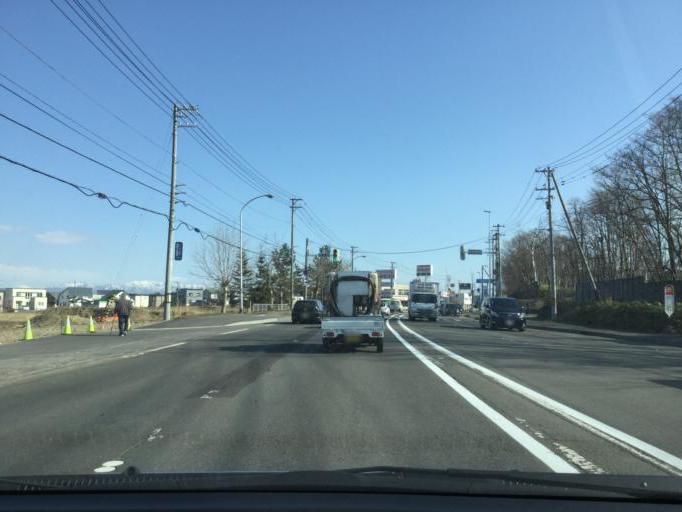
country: JP
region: Hokkaido
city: Iwamizawa
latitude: 43.2141
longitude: 141.7844
